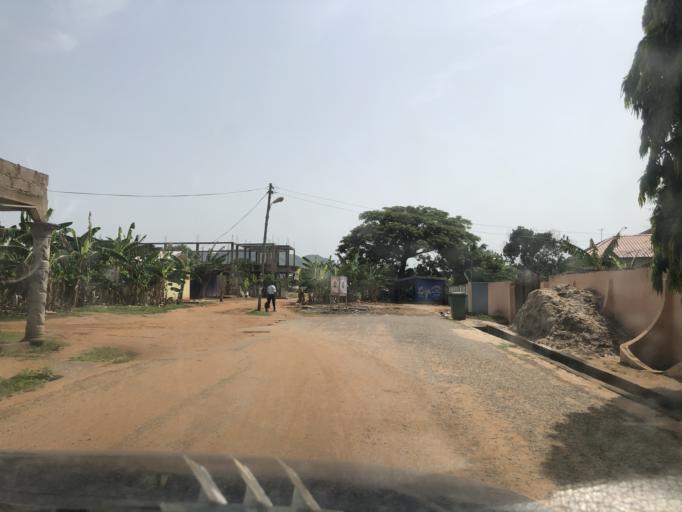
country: GH
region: Eastern
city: Koforidua
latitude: 6.0926
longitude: -0.2724
